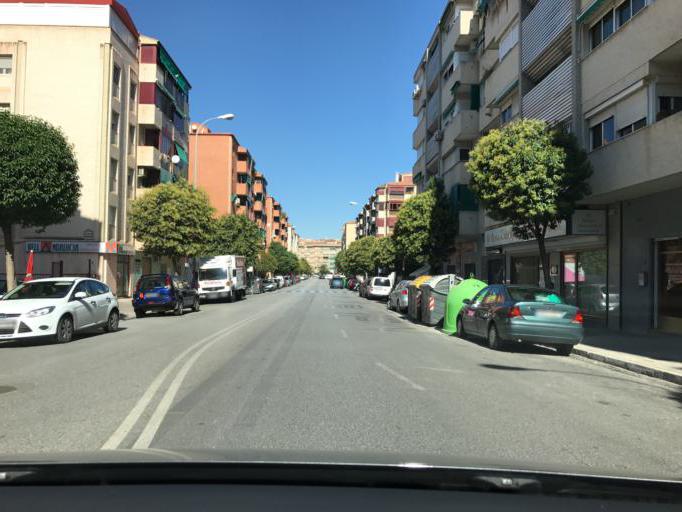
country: ES
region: Andalusia
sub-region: Provincia de Granada
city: Granada
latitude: 37.1629
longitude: -3.6025
